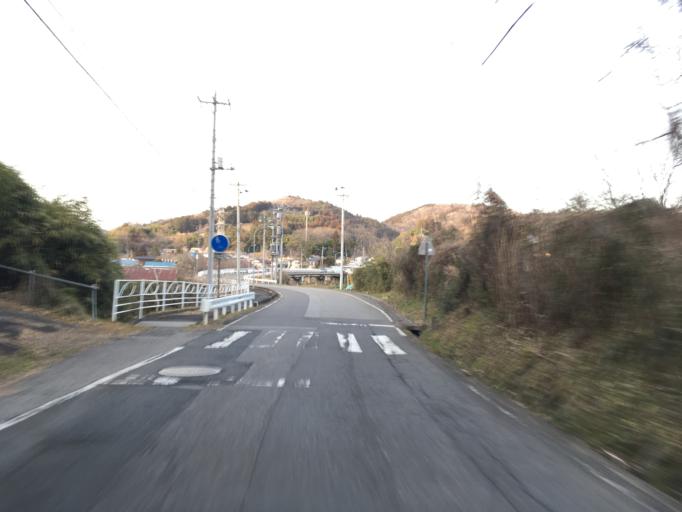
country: JP
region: Ibaraki
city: Daigo
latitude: 36.8134
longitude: 140.3696
